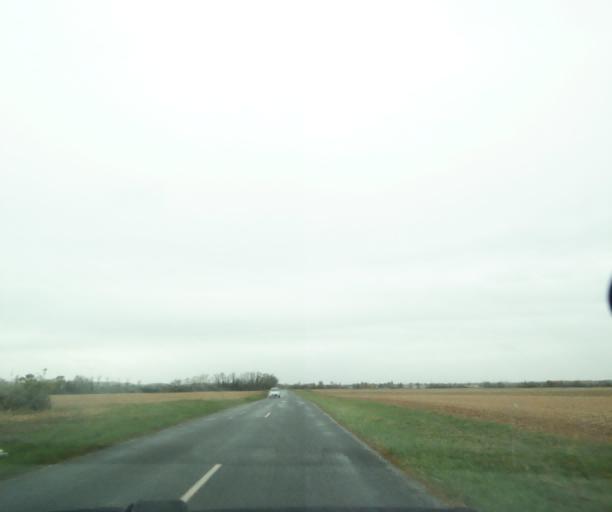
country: FR
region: Rhone-Alpes
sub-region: Departement de l'Ain
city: Loyettes
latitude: 45.7884
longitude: 5.2223
